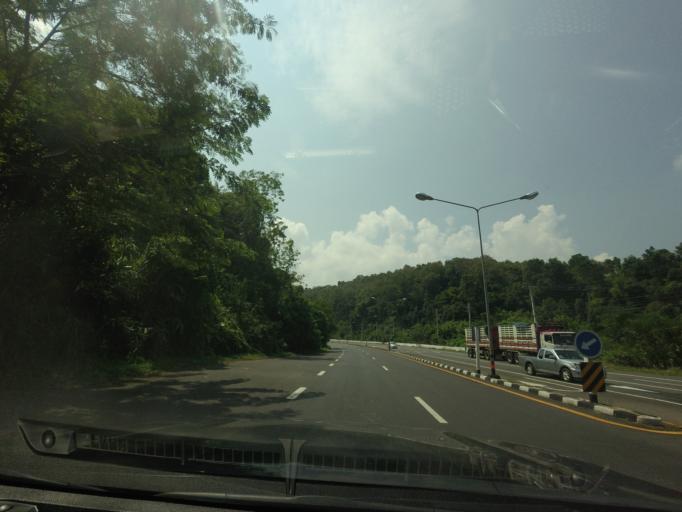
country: TH
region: Phrae
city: Den Chai
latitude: 17.8787
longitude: 100.0455
